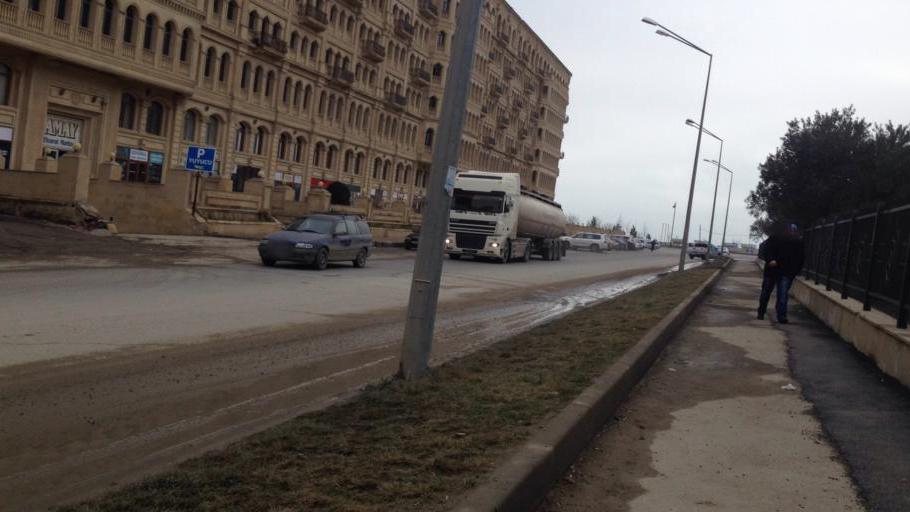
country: AZ
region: Baki
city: Baku
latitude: 40.3806
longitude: 49.8771
